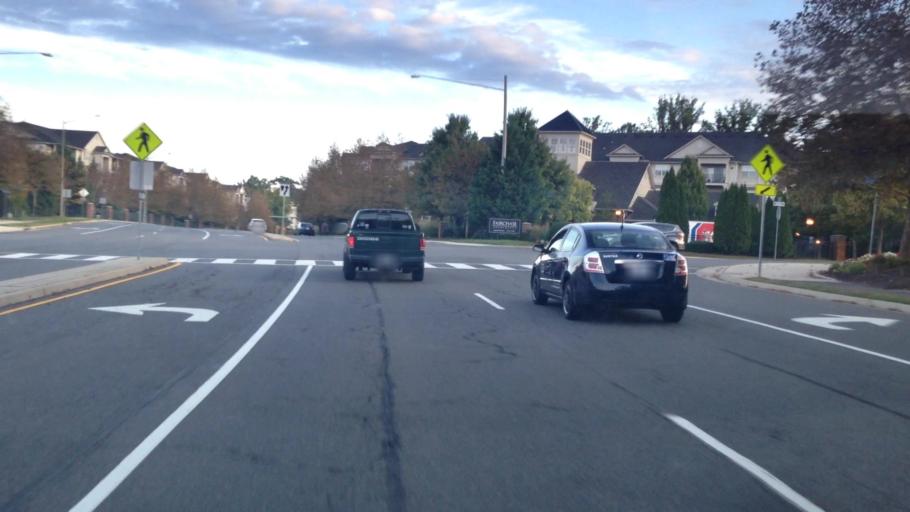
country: US
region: Virginia
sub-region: Fairfax County
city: Greenbriar
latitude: 38.8525
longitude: -77.3645
